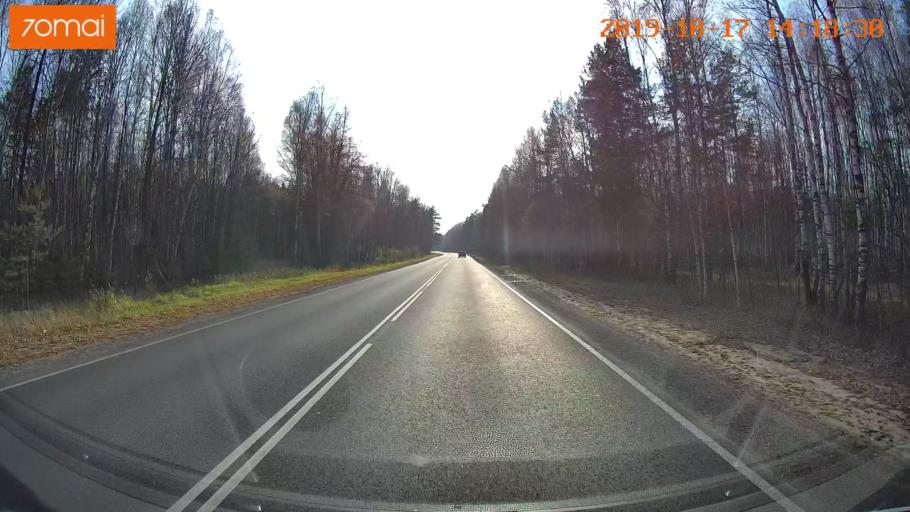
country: RU
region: Rjazan
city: Spas-Klepiki
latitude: 55.0624
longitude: 40.0298
